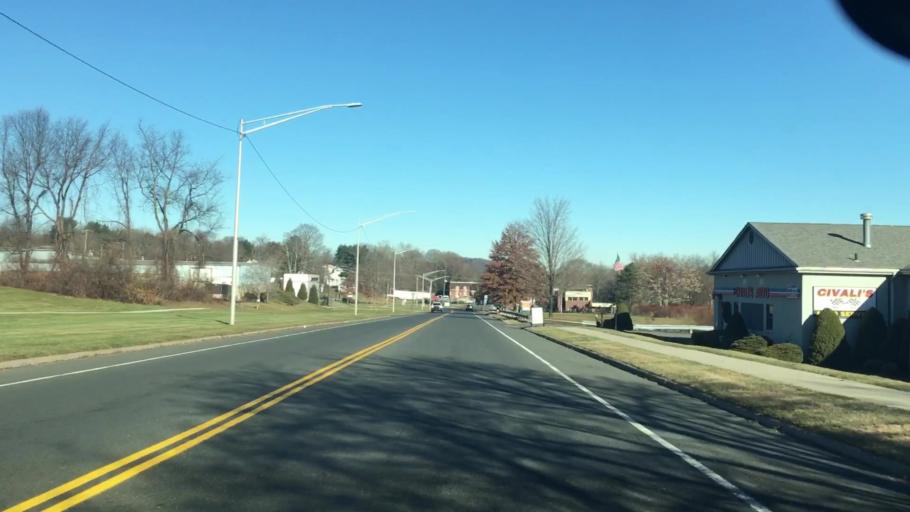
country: US
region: Connecticut
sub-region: New Haven County
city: Meriden
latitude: 41.5226
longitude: -72.7600
